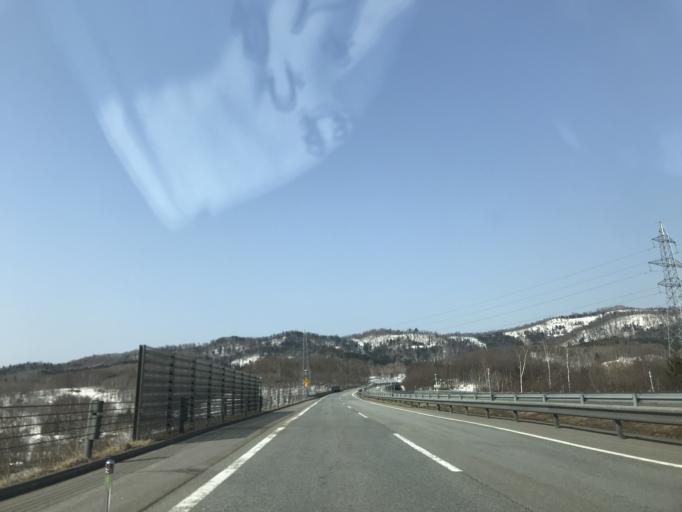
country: JP
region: Hokkaido
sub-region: Asahikawa-shi
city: Asahikawa
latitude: 43.7941
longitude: 142.2834
